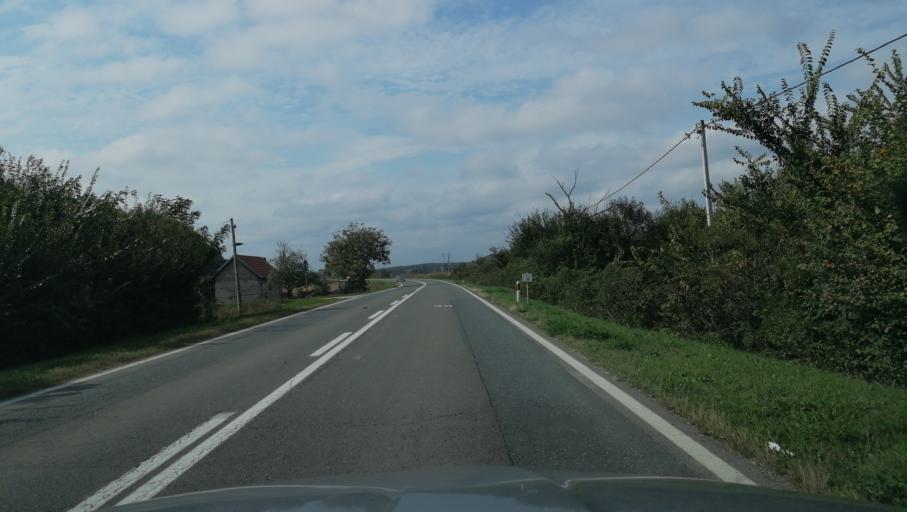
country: RS
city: Bosut
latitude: 44.9250
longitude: 19.3351
